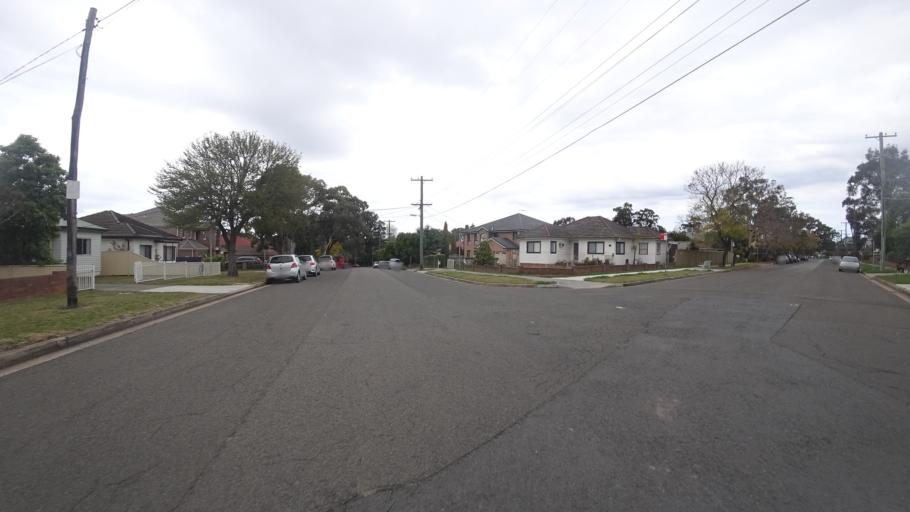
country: AU
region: New South Wales
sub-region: Liverpool
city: East Hills
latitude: -33.9608
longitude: 150.9867
